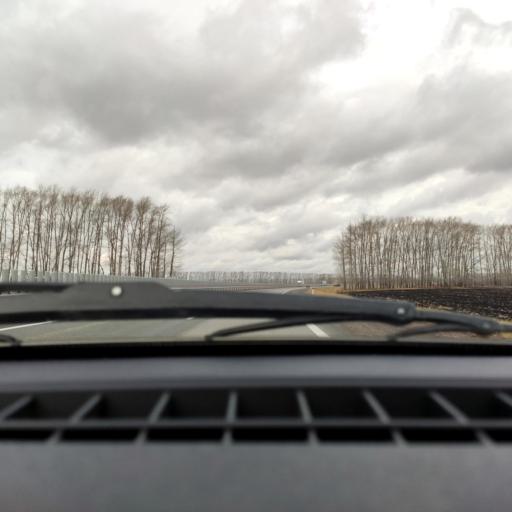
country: RU
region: Bashkortostan
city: Asanovo
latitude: 54.9249
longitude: 55.5778
